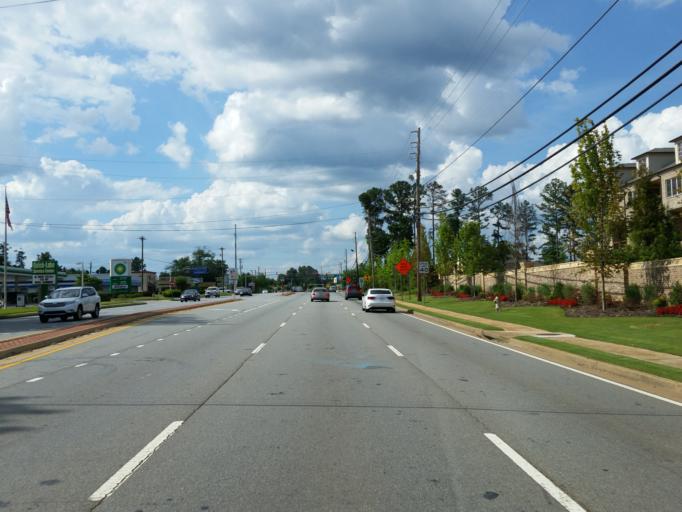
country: US
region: Georgia
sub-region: Fulton County
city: Sandy Springs
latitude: 33.9619
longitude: -84.4116
